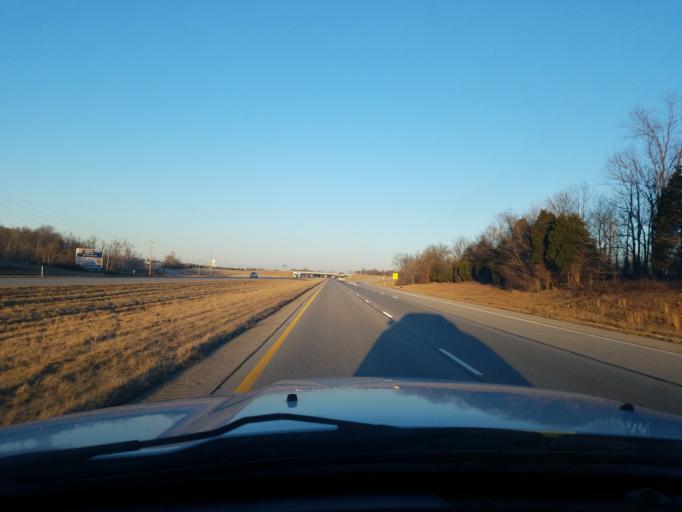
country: US
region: Indiana
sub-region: Floyd County
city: Georgetown
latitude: 38.2610
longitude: -86.0075
